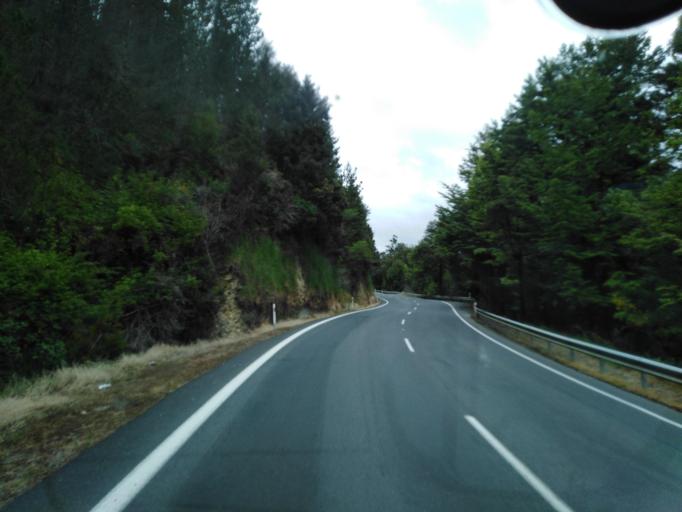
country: NZ
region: Tasman
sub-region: Tasman District
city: Wakefield
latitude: -41.6245
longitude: 172.7297
